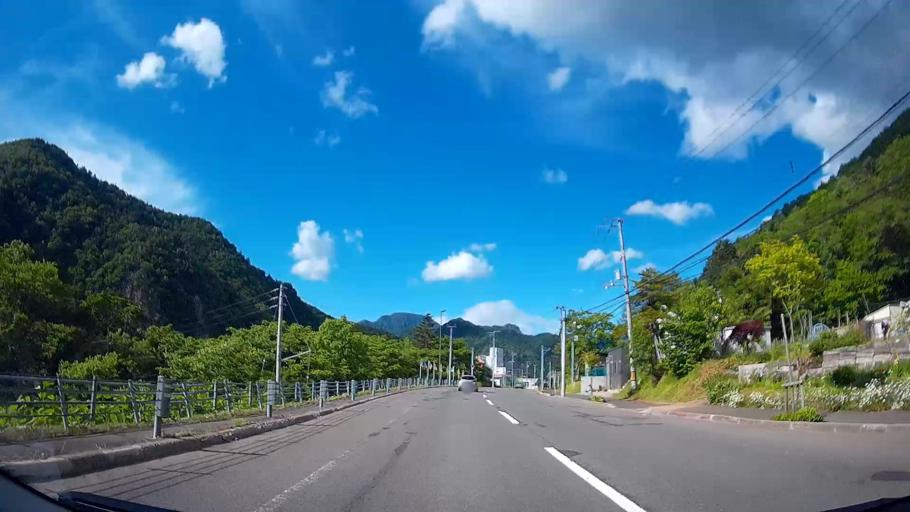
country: JP
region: Hokkaido
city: Sapporo
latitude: 42.9596
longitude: 141.1568
